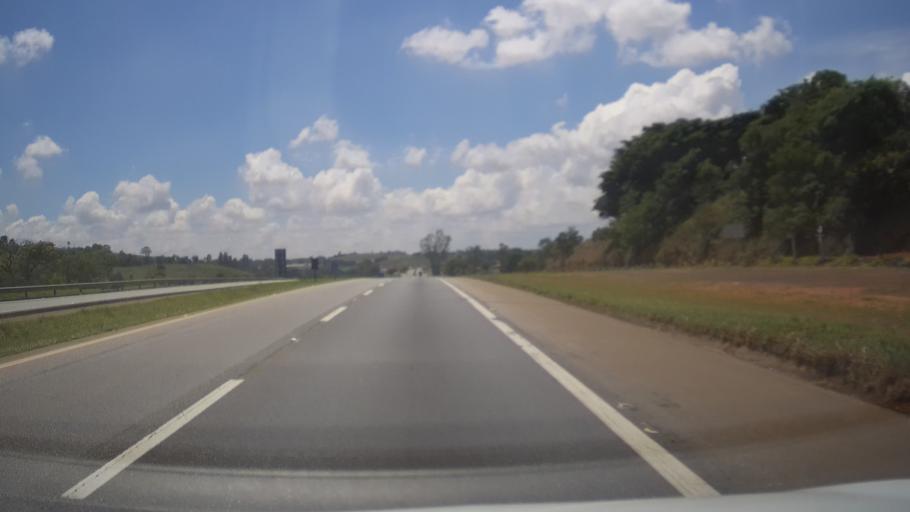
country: BR
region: Minas Gerais
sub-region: Sao Goncalo Do Sapucai
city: Sao Goncalo do Sapucai
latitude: -21.9176
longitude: -45.5911
